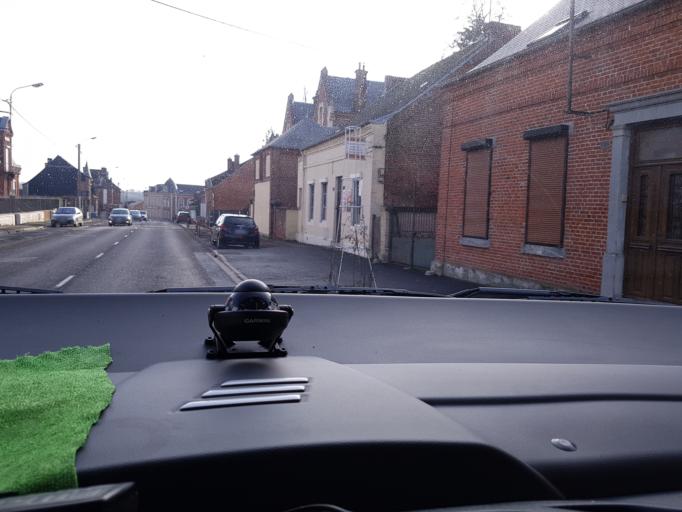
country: FR
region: Picardie
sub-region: Departement de l'Aisne
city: Hirson
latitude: 49.9277
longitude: 4.0754
